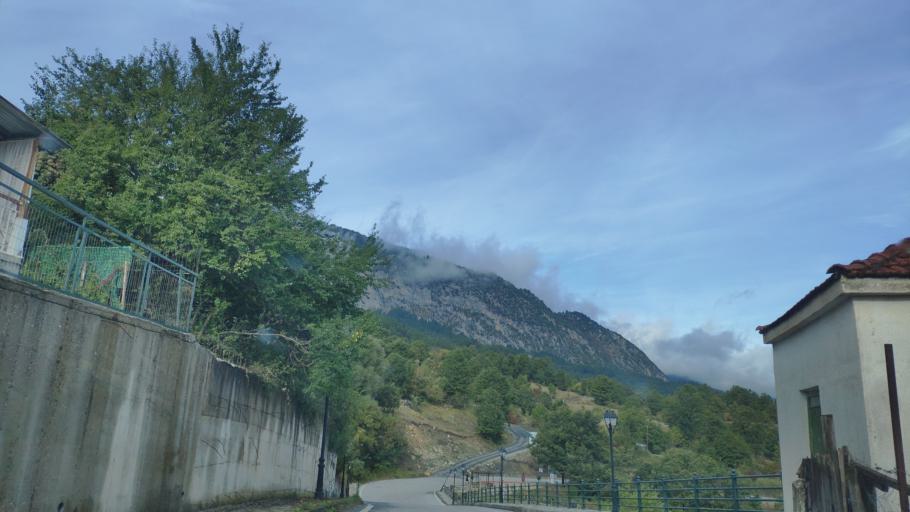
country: GR
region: West Macedonia
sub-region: Nomos Kastorias
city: Nestorio
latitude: 40.2758
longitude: 20.9752
